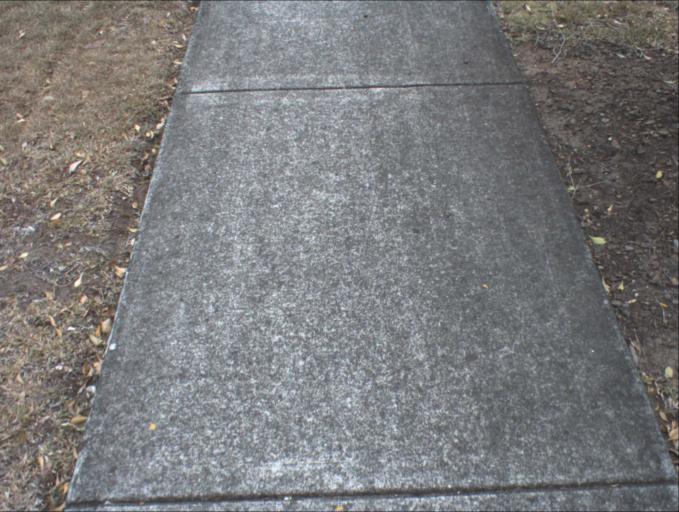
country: AU
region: Queensland
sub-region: Logan
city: Slacks Creek
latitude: -27.6696
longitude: 153.1885
